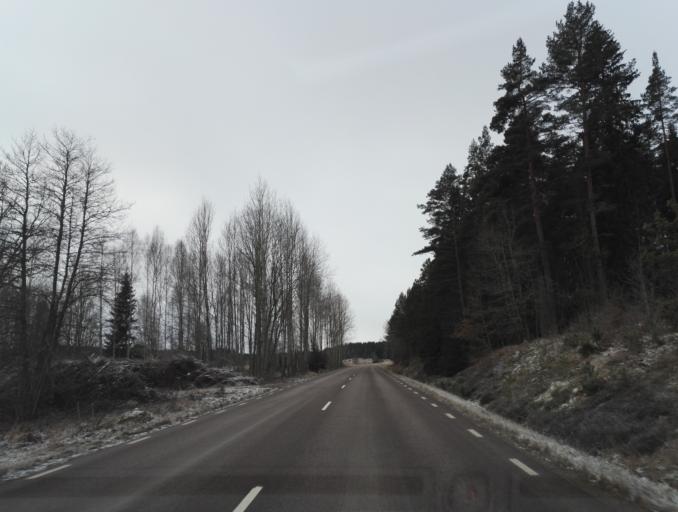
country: SE
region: Kalmar
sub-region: Hultsfreds Kommun
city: Virserum
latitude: 57.3550
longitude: 15.6118
